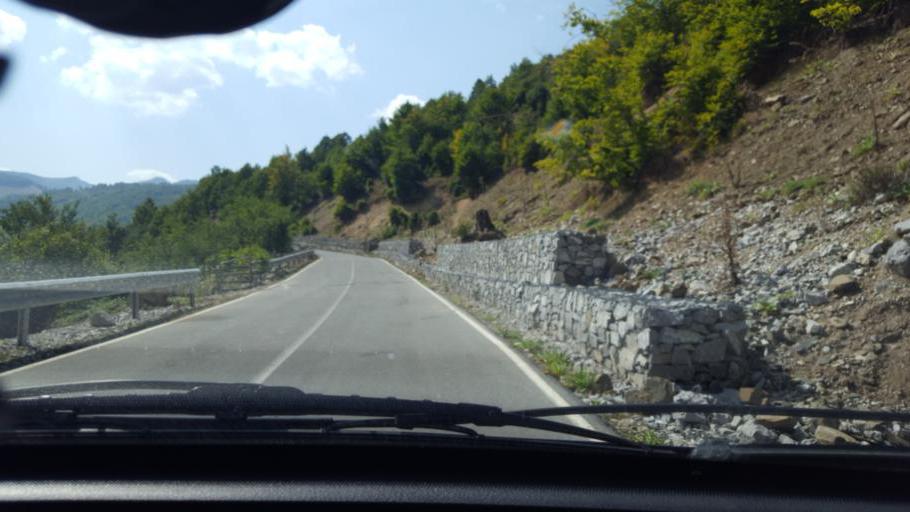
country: ME
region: Andrijevica
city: Andrijevica
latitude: 42.5536
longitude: 19.7252
